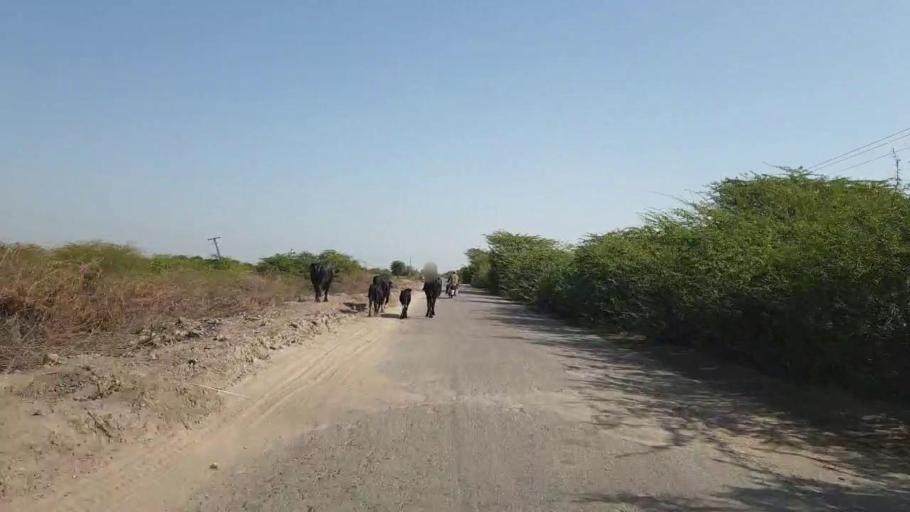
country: PK
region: Sindh
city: Chor
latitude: 25.4736
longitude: 69.7723
